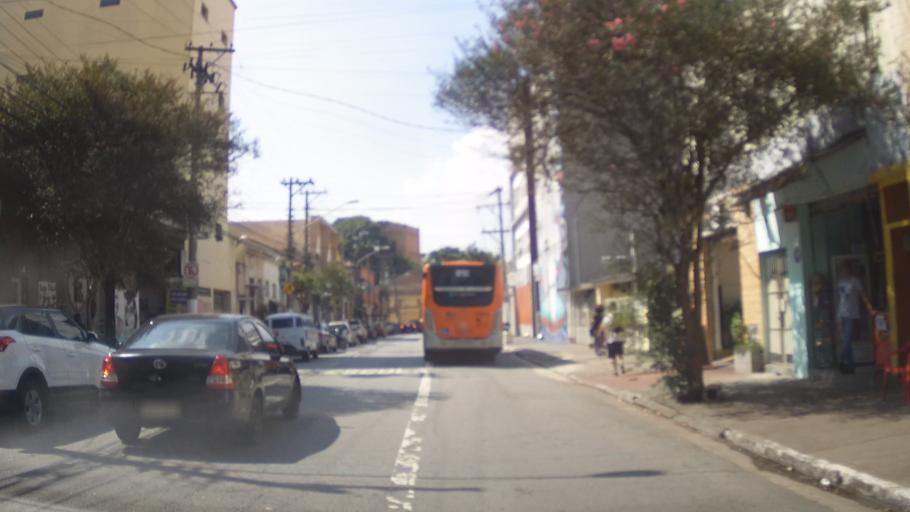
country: BR
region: Sao Paulo
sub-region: Sao Paulo
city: Sao Paulo
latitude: -23.5225
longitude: -46.6992
